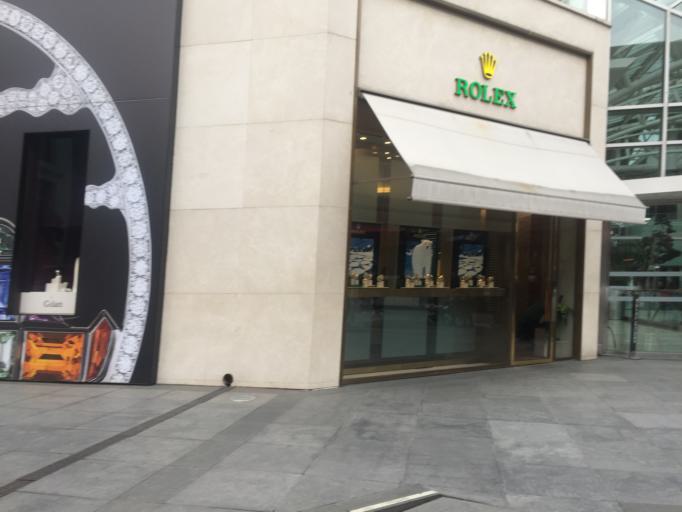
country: TR
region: Istanbul
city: Sisli
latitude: 41.1100
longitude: 29.0314
